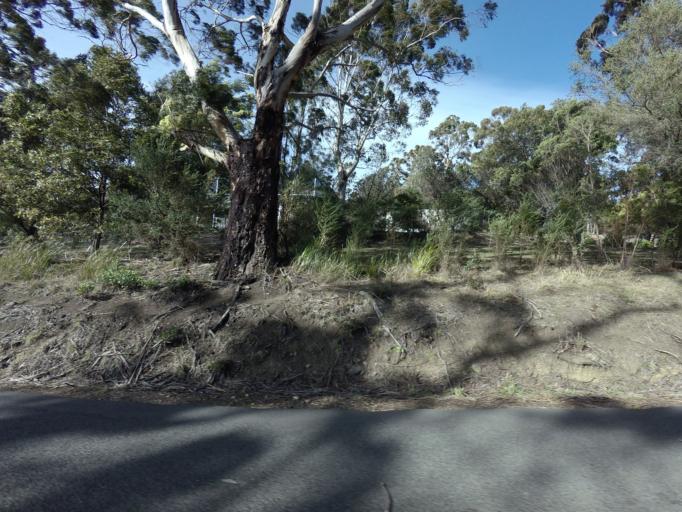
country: AU
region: Tasmania
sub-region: Kingborough
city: Kettering
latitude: -43.1652
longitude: 147.2190
